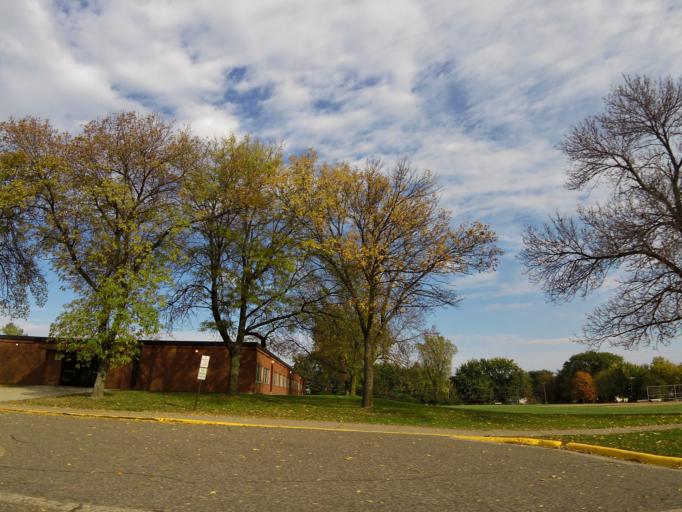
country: US
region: Minnesota
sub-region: Dakota County
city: Eagan
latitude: 44.8048
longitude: -93.2157
